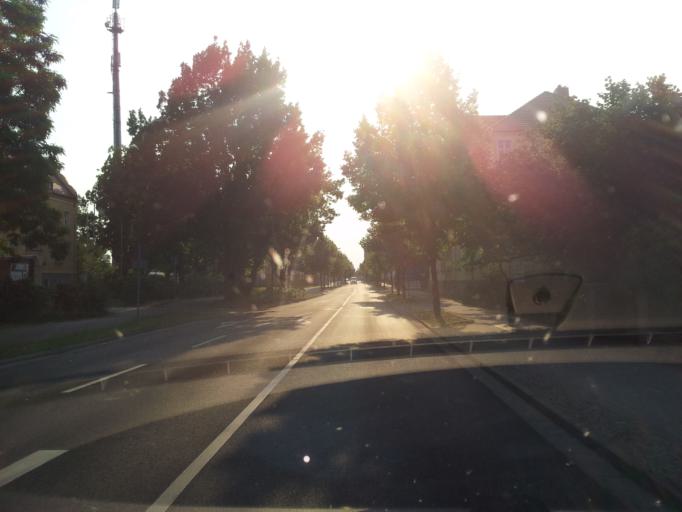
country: DE
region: Saxony
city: Hoyerswerda
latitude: 51.4353
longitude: 14.2441
